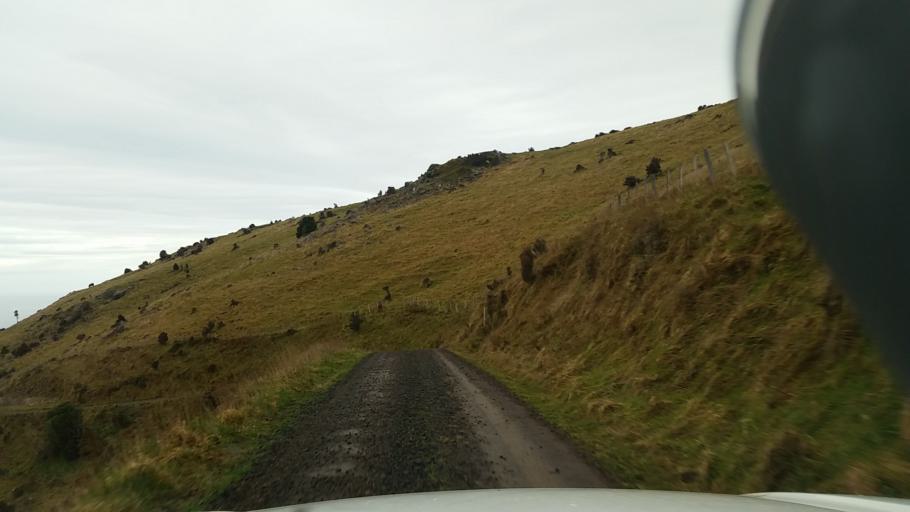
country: NZ
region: Canterbury
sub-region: Christchurch City
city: Christchurch
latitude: -43.7386
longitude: 173.0203
